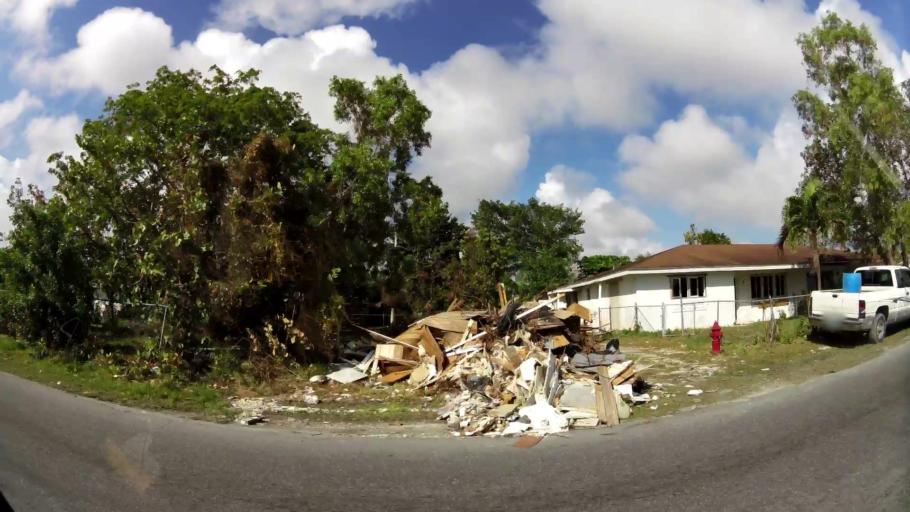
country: BS
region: Freeport
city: Lucaya
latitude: 26.5221
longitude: -78.6815
